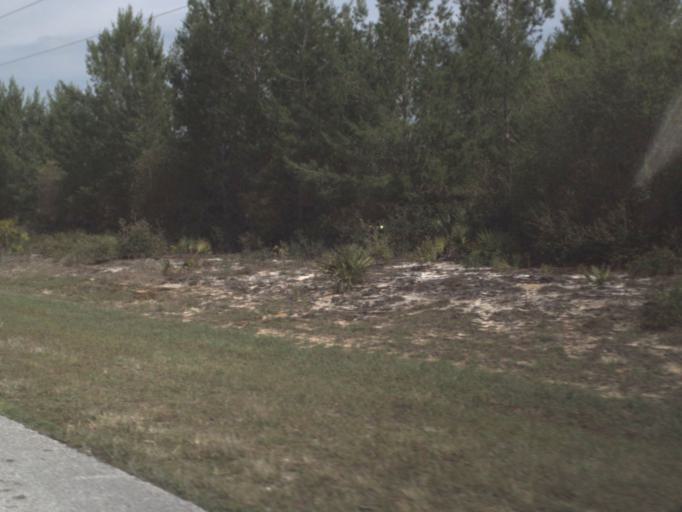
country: US
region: Florida
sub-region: Putnam County
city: Crescent City
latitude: 29.3273
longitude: -81.7073
